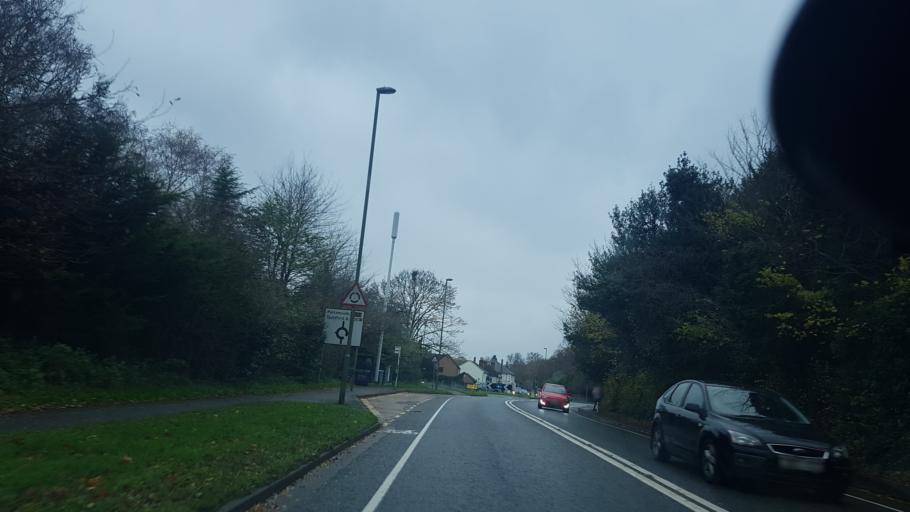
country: GB
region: England
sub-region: Surrey
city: Guildford
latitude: 51.2565
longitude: -0.5474
